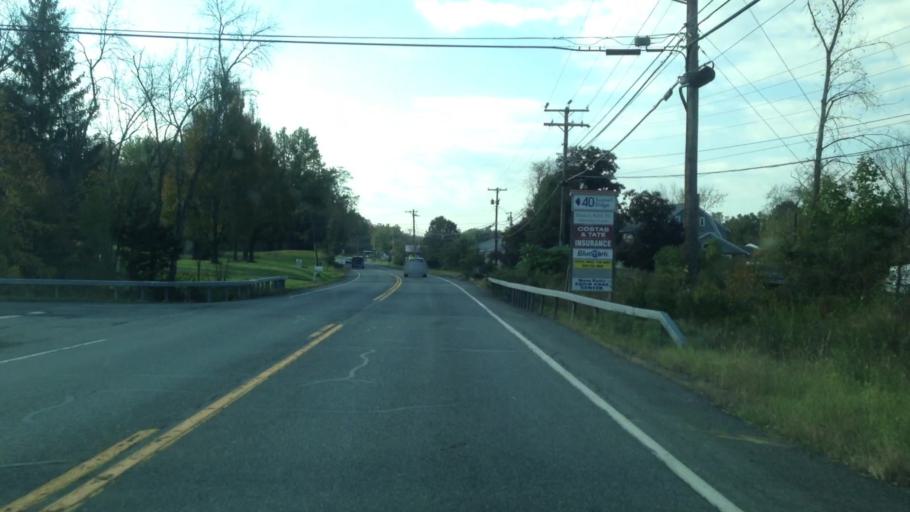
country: US
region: New York
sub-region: Ulster County
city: New Paltz
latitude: 41.7608
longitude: -74.0814
